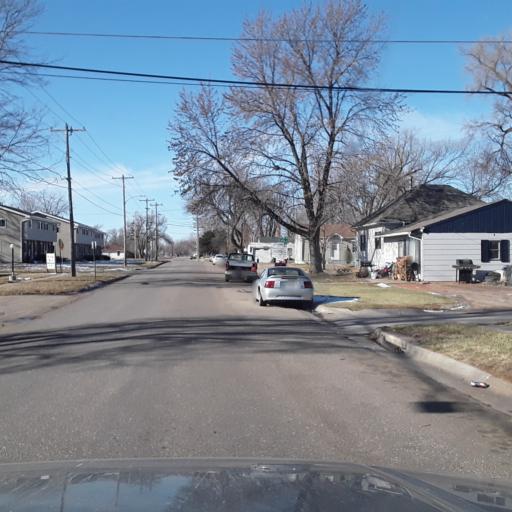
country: US
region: Nebraska
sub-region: Adams County
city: Hastings
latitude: 40.5771
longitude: -98.3999
